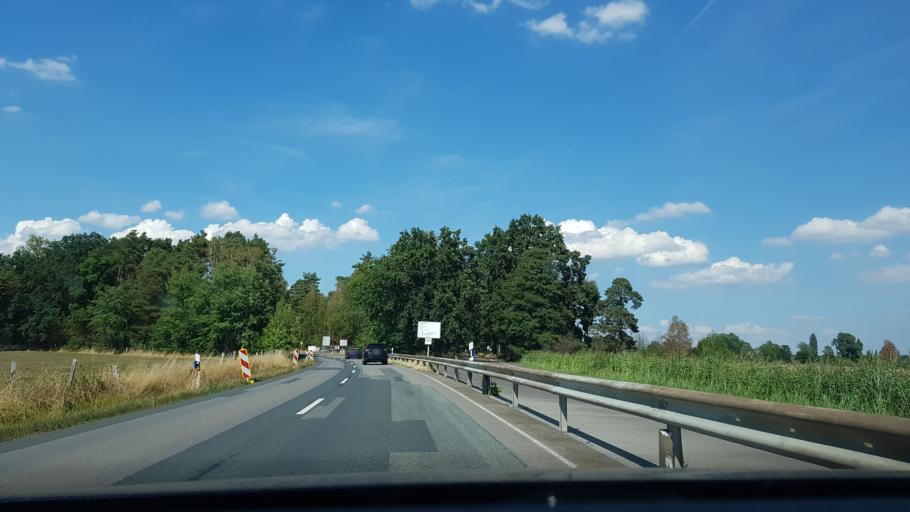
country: DE
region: Lower Saxony
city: Isenbuttel
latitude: 52.4438
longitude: 10.6075
